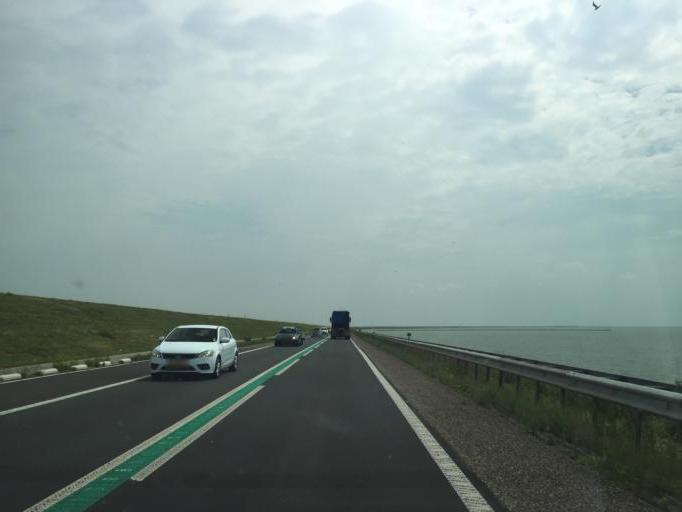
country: NL
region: North Holland
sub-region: Gemeente Enkhuizen
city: Enkhuizen
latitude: 52.6817
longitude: 5.3374
